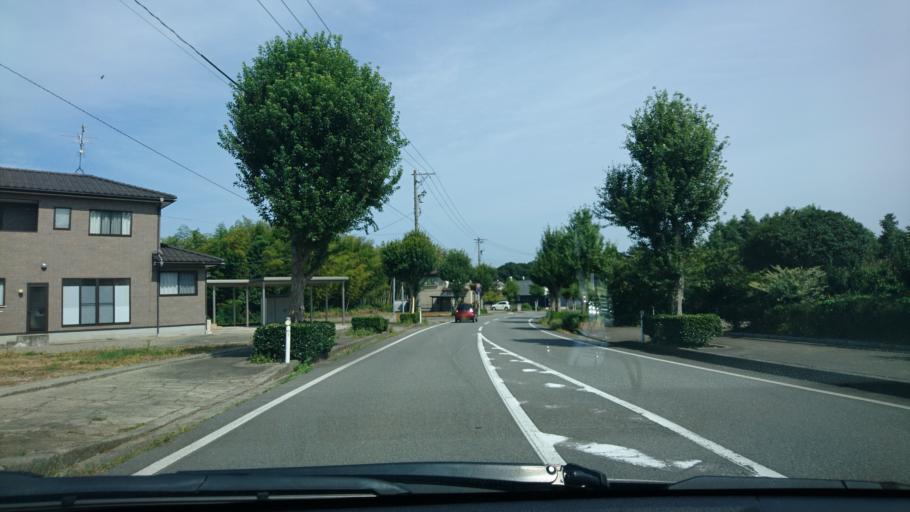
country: JP
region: Ishikawa
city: Komatsu
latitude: 36.3296
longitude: 136.3481
